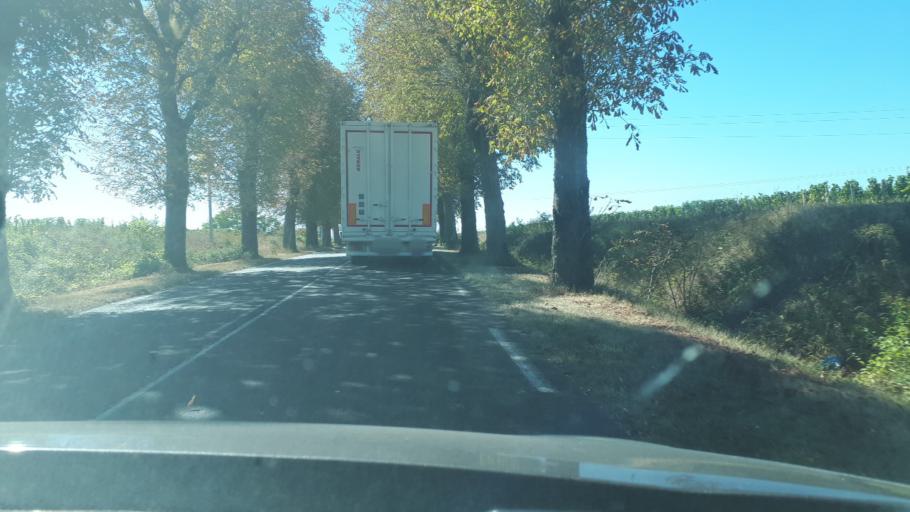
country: FR
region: Centre
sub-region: Departement du Cher
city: Sancerre
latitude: 47.3190
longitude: 2.8166
